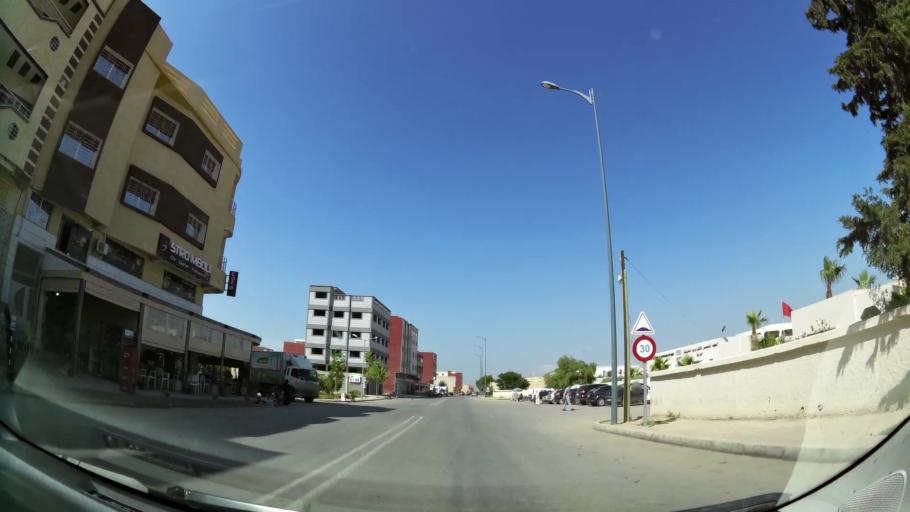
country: MA
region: Oriental
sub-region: Oujda-Angad
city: Oujda
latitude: 34.6950
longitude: -1.8812
